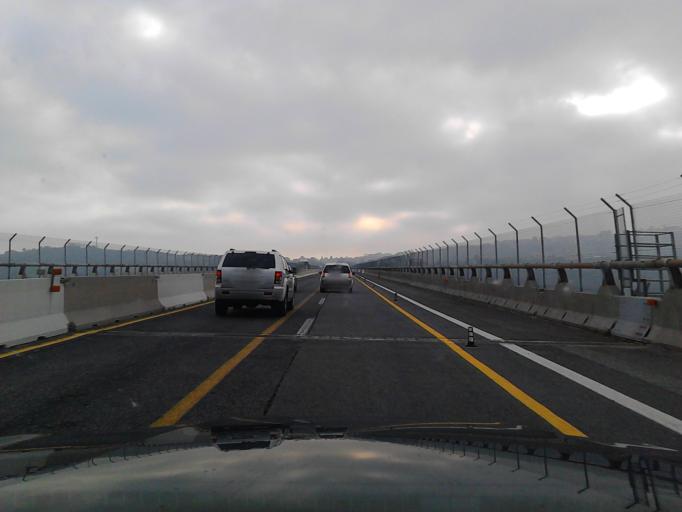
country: IT
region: Abruzzo
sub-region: Provincia di Teramo
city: Salino
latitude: 42.7802
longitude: 13.9336
